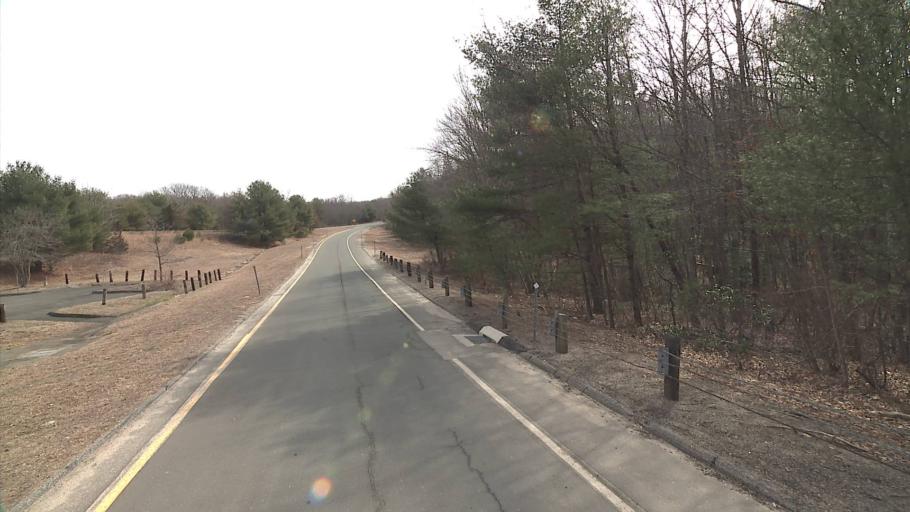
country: US
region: Connecticut
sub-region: Middlesex County
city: Higganum
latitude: 41.4558
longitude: -72.5289
